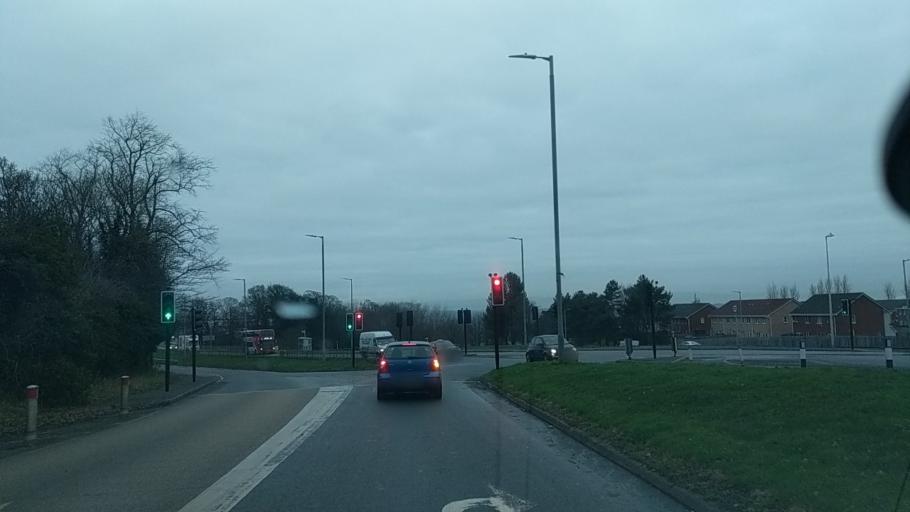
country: GB
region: Scotland
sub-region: South Lanarkshire
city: Rutherglen
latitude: 55.8089
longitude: -4.1845
